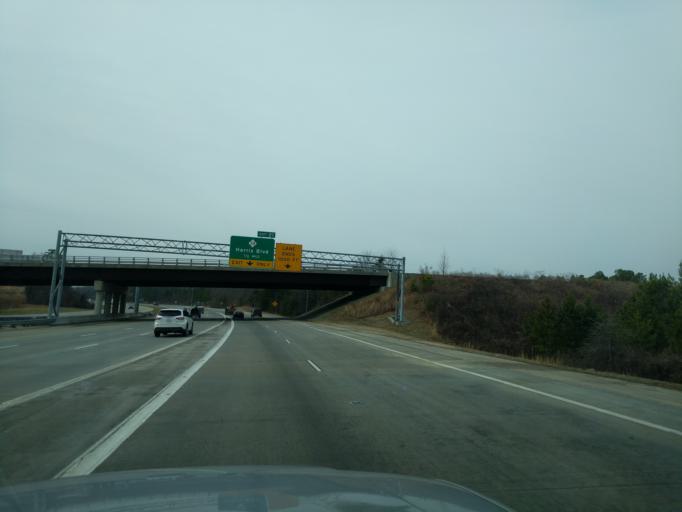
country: US
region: North Carolina
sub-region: Mecklenburg County
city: Huntersville
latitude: 35.3623
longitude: -80.8525
